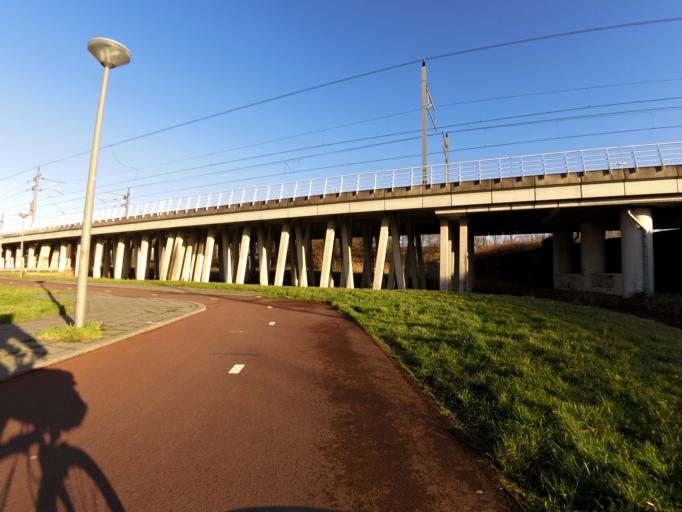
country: NL
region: South Holland
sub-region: Gemeente Rotterdam
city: Delfshaven
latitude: 51.9355
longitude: 4.4499
